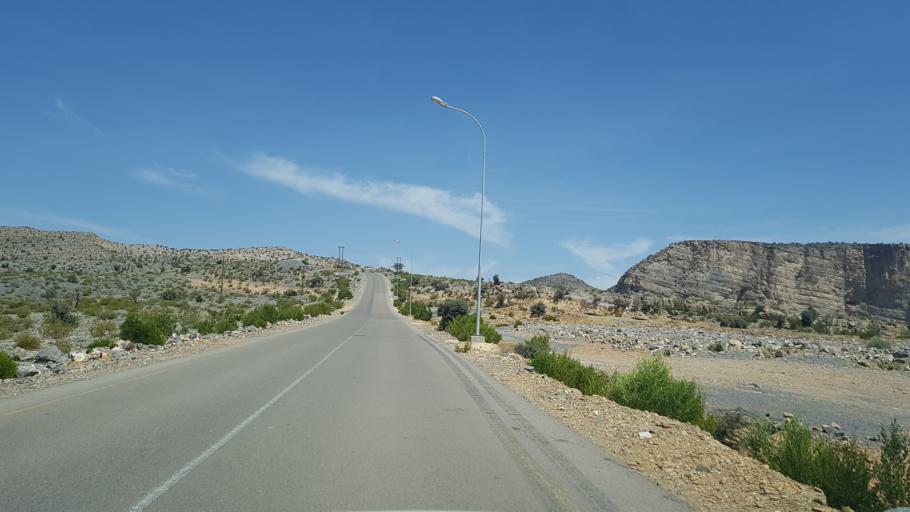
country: OM
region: Al Batinah
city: Bayt al `Awabi
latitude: 23.1373
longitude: 57.5464
